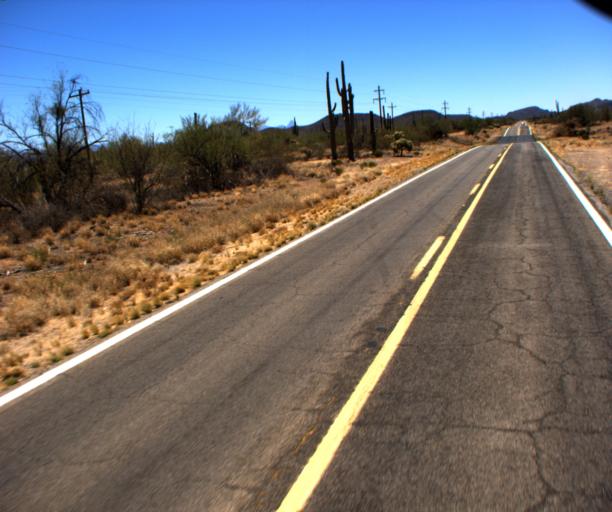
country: US
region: Arizona
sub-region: Pima County
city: Sells
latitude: 32.0079
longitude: -111.9916
